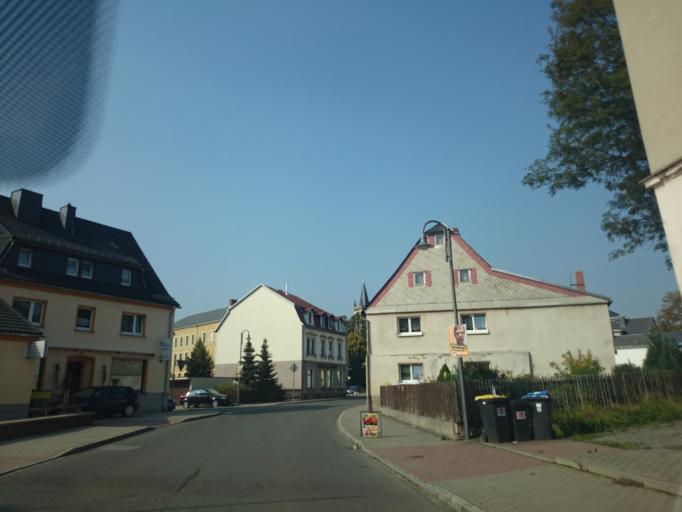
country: DE
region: Saxony
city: Eppendorf
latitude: 50.7980
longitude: 13.2278
